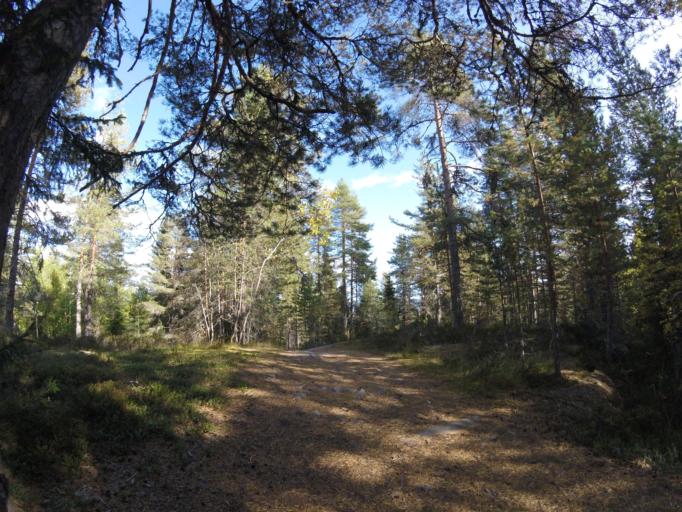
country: NO
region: Buskerud
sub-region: Kongsberg
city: Kongsberg
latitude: 59.6668
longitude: 9.6054
